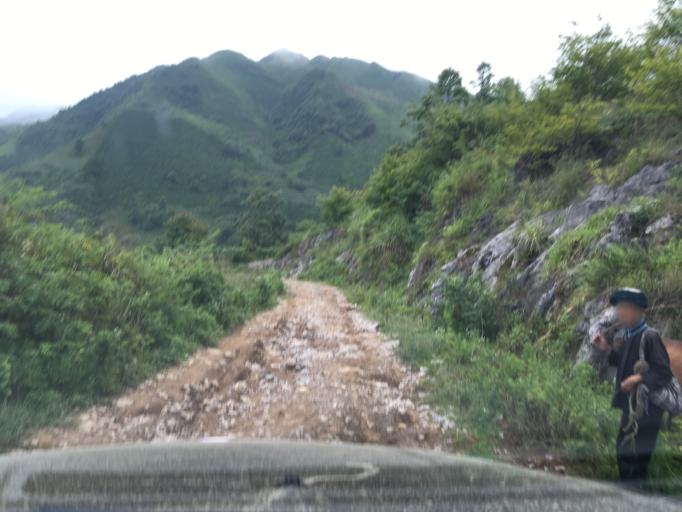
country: CN
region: Guangxi Zhuangzu Zizhiqu
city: Xinzhou
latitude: 24.9911
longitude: 105.6381
